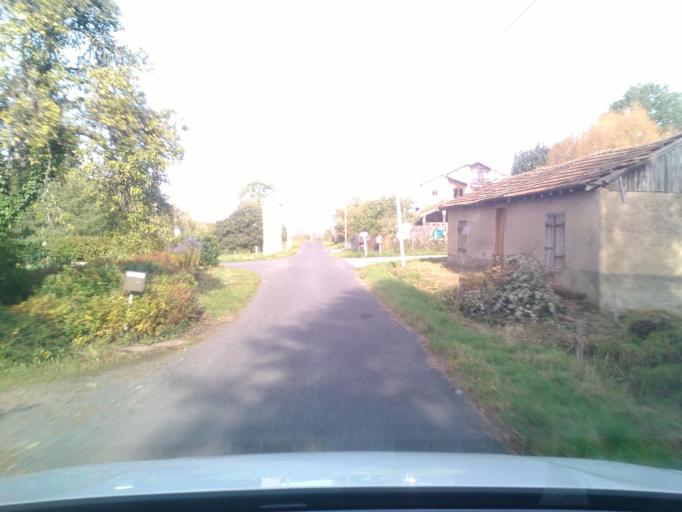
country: FR
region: Lorraine
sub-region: Departement des Vosges
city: Senones
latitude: 48.3525
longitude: 7.0214
